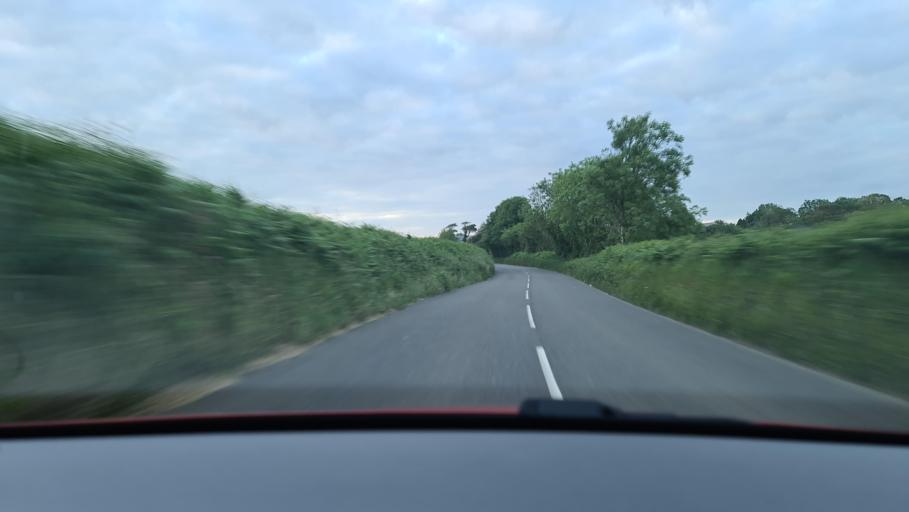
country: GB
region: England
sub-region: Cornwall
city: Liskeard
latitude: 50.4184
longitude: -4.4341
